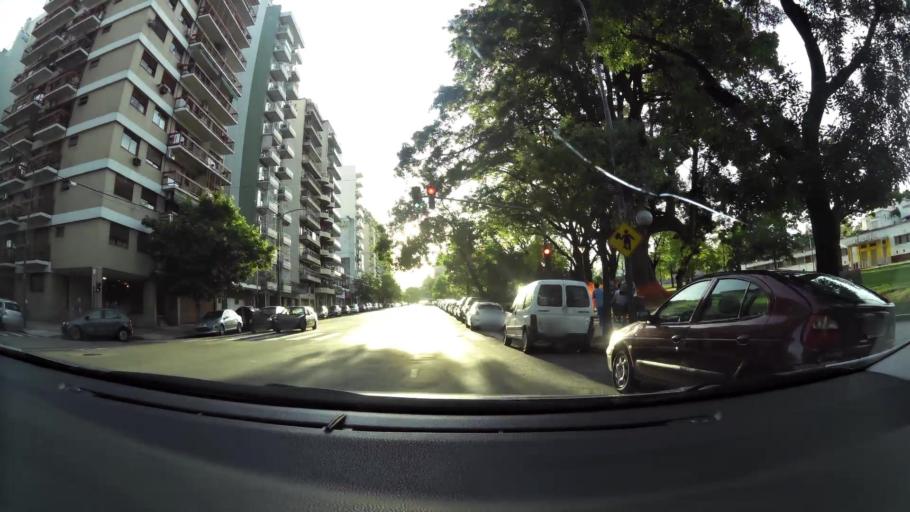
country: AR
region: Buenos Aires F.D.
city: Villa Santa Rita
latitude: -34.6360
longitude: -58.4427
